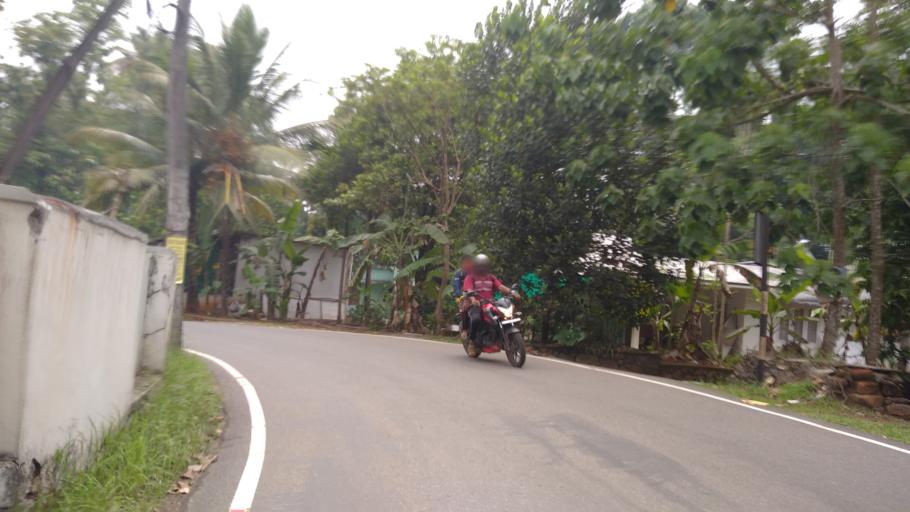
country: IN
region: Kerala
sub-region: Ernakulam
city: Perumpavur
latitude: 10.1189
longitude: 76.5312
